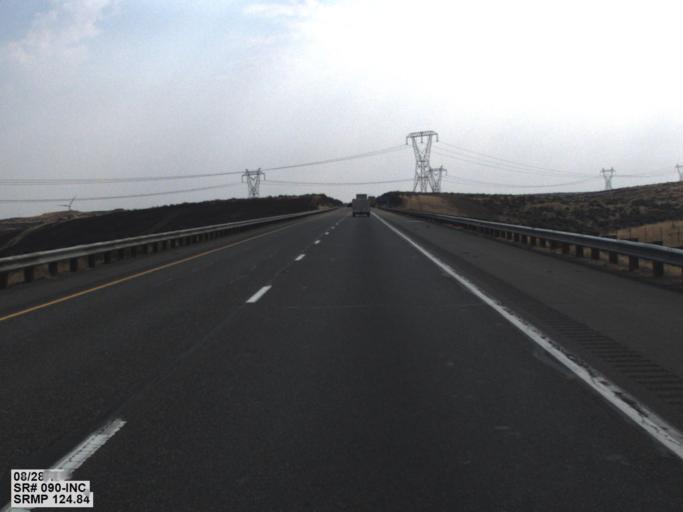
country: US
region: Washington
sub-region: Kittitas County
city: Kittitas
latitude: 46.9431
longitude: -120.2254
